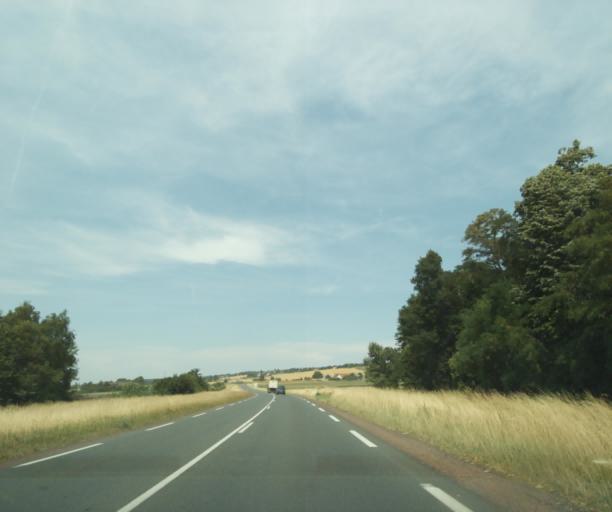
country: FR
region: Poitou-Charentes
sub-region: Departement de la Vienne
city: Chatellerault
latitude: 46.7937
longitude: 0.5584
